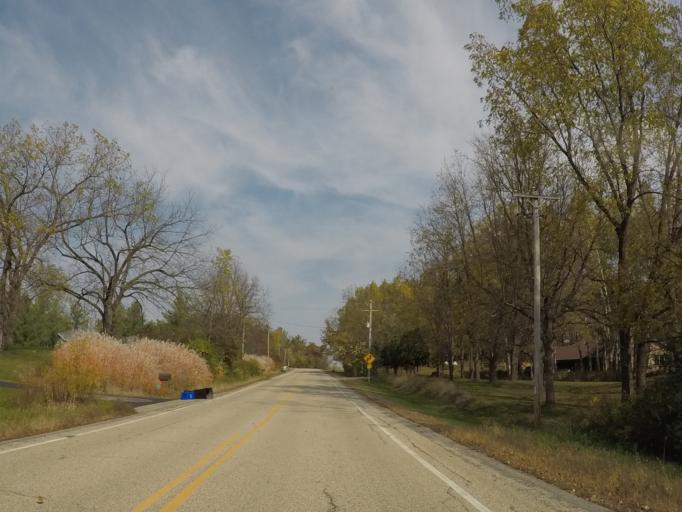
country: US
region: Wisconsin
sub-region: Dane County
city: Cross Plains
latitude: 43.0270
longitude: -89.6215
